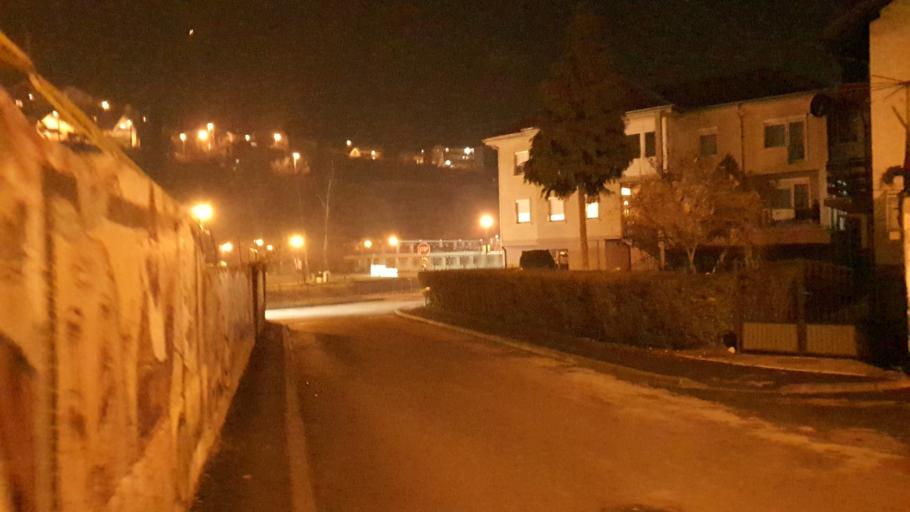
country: RS
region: Central Serbia
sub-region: Zlatiborski Okrug
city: Uzice
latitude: 43.8548
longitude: 19.8348
